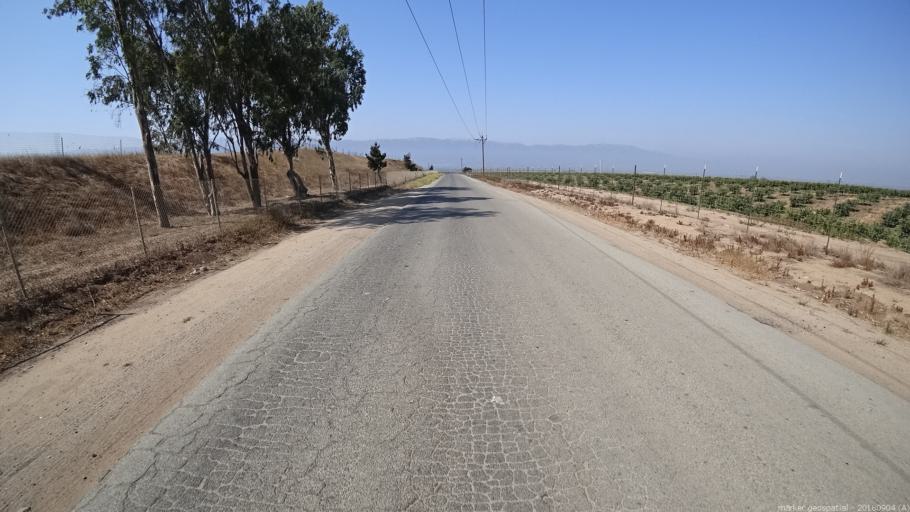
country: US
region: California
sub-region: Monterey County
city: Gonzales
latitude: 36.5324
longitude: -121.4083
